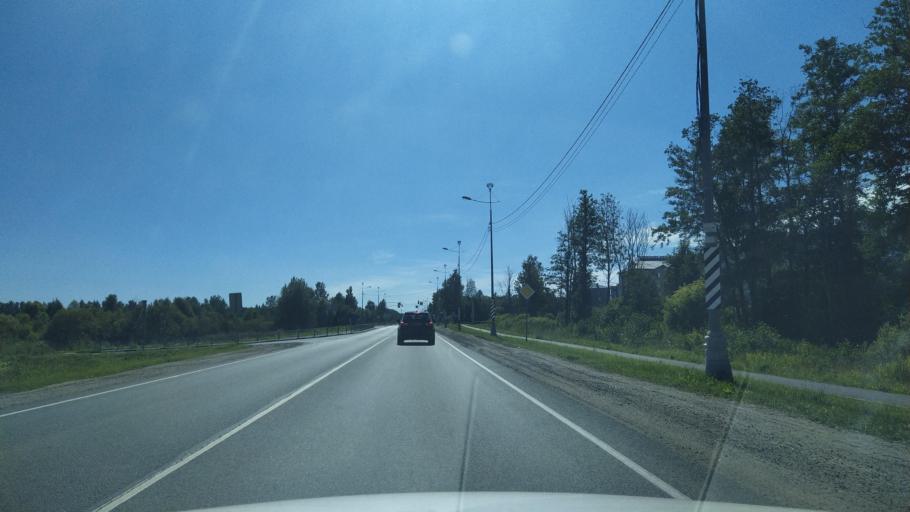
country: RU
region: Pskov
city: Pskov
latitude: 57.7921
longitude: 28.4143
